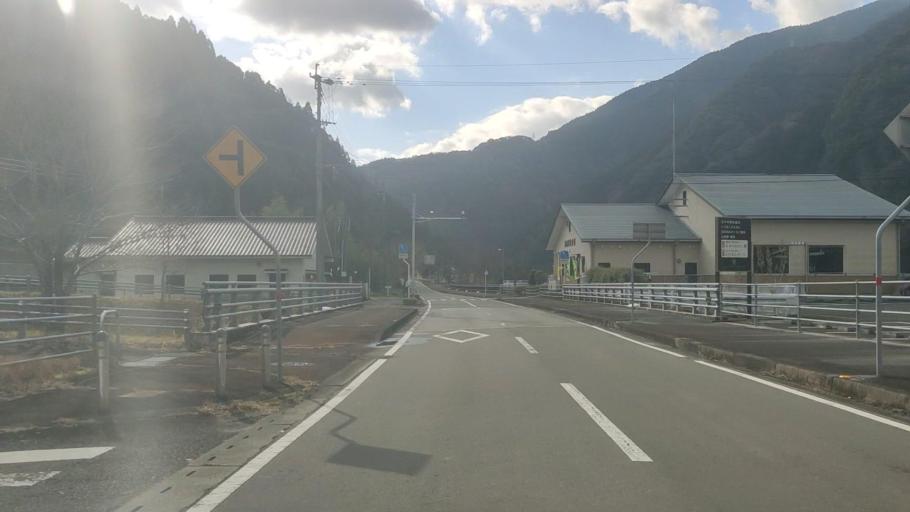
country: JP
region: Kumamoto
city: Hitoyoshi
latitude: 32.3965
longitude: 130.8267
